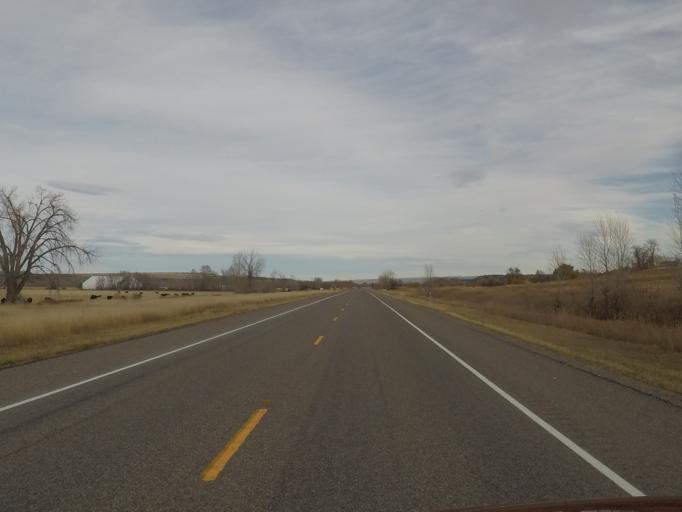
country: US
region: Montana
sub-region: Stillwater County
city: Columbus
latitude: 45.4598
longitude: -109.0607
